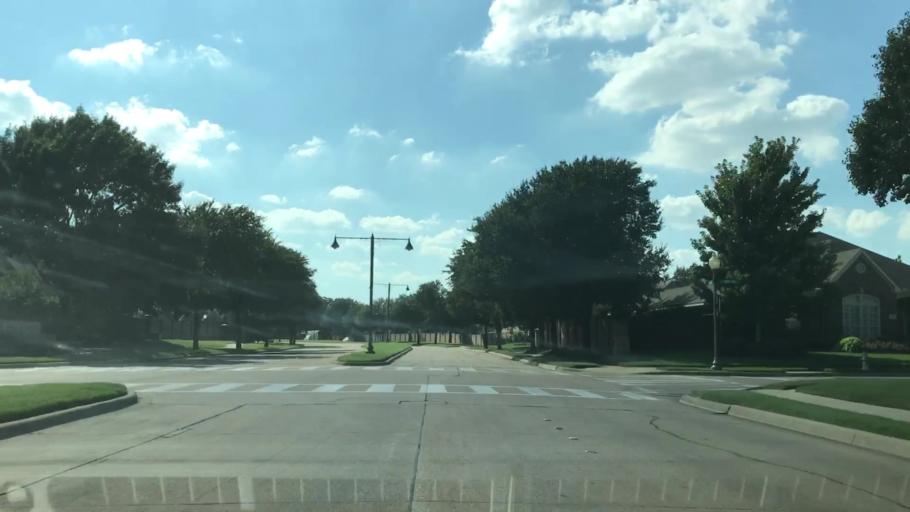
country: US
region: Texas
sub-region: Tarrant County
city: Colleyville
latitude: 32.9234
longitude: -97.1888
